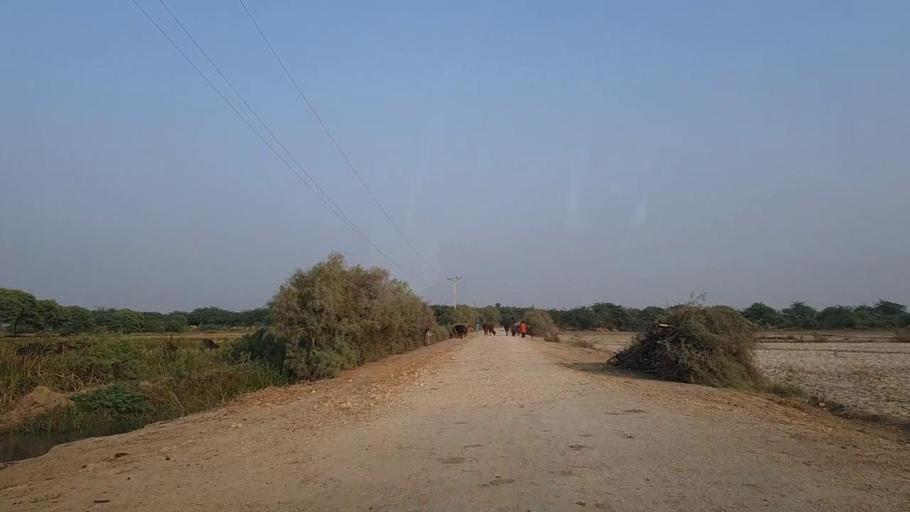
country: PK
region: Sindh
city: Thatta
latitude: 24.6920
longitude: 67.8071
